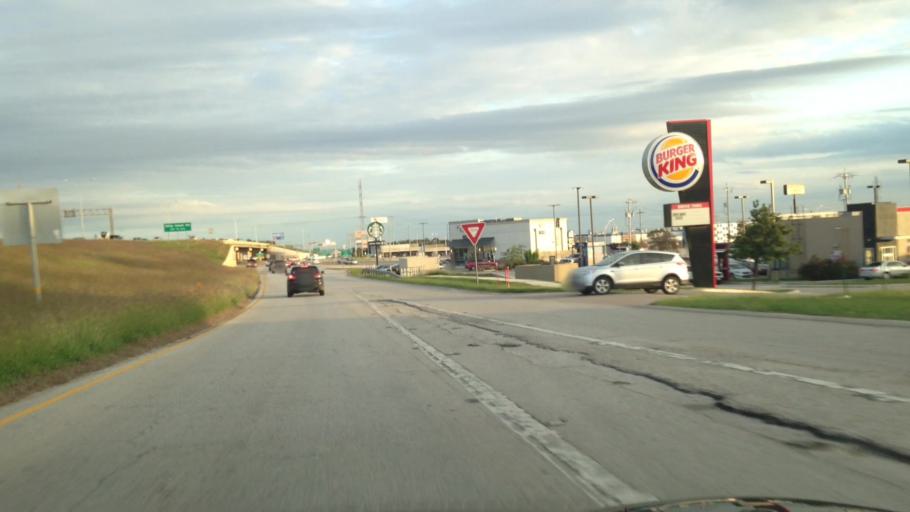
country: US
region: Texas
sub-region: Bexar County
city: Live Oak
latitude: 29.5632
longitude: -98.3297
